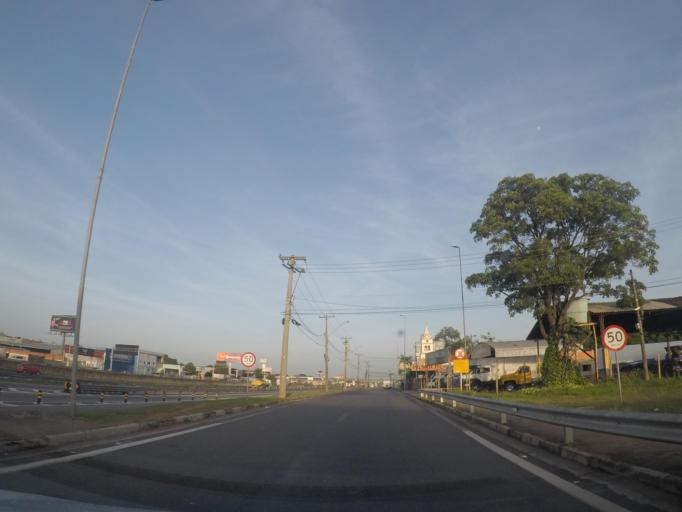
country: BR
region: Sao Paulo
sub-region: Hortolandia
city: Hortolandia
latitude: -22.8573
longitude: -47.1470
